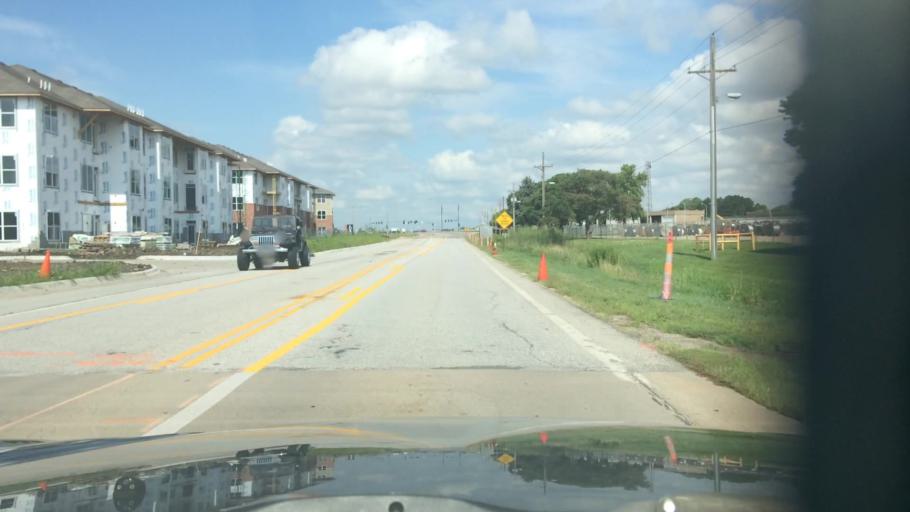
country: US
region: Nebraska
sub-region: Sarpy County
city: Papillion
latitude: 41.1633
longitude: -96.0570
